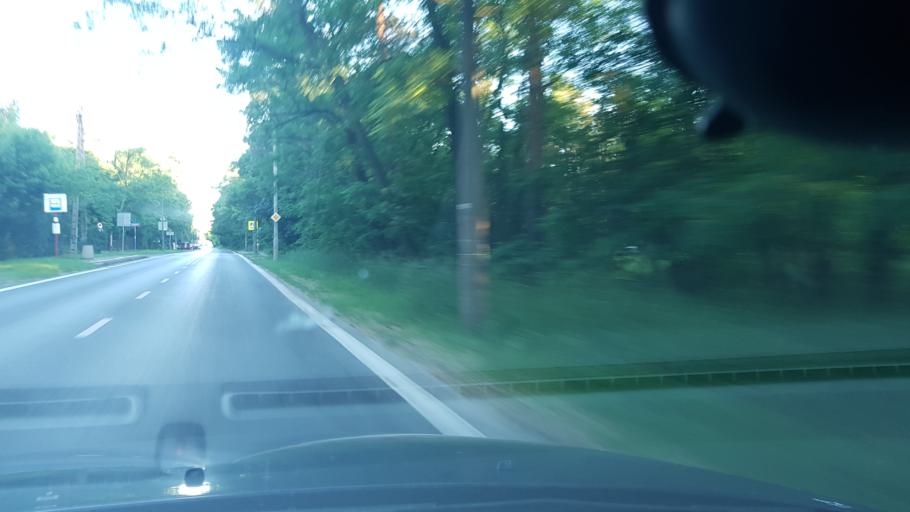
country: PL
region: Masovian Voivodeship
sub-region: Powiat otwocki
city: Jozefow
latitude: 52.1665
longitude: 21.2069
